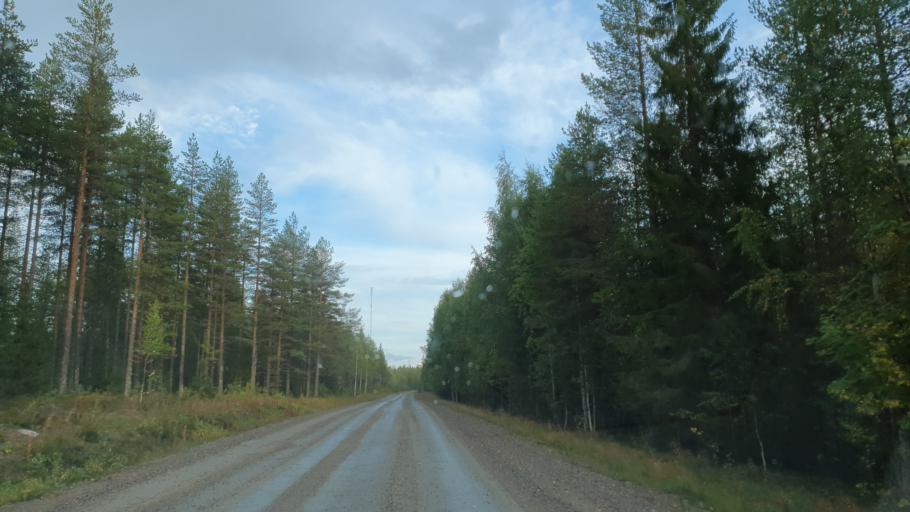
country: FI
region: Kainuu
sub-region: Kehys-Kainuu
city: Kuhmo
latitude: 64.4157
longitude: 29.5097
